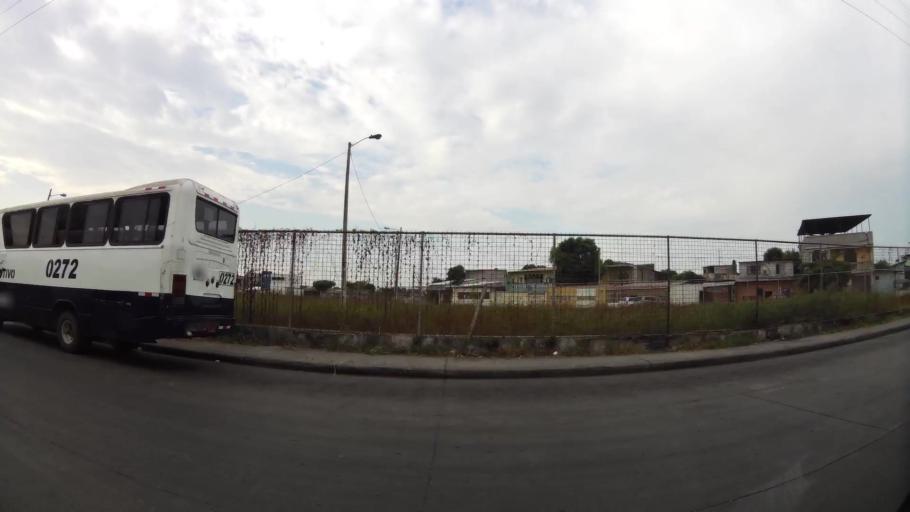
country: EC
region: Guayas
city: Guayaquil
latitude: -2.2556
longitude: -79.8760
